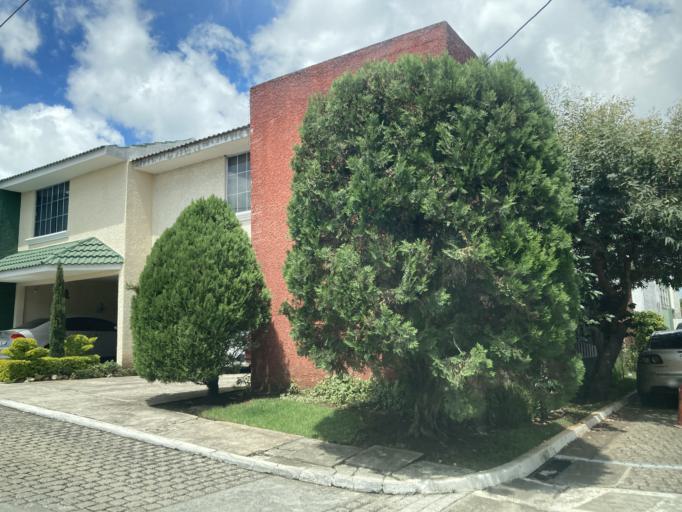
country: GT
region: Guatemala
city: San Jose Pinula
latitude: 14.5418
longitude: -90.4347
